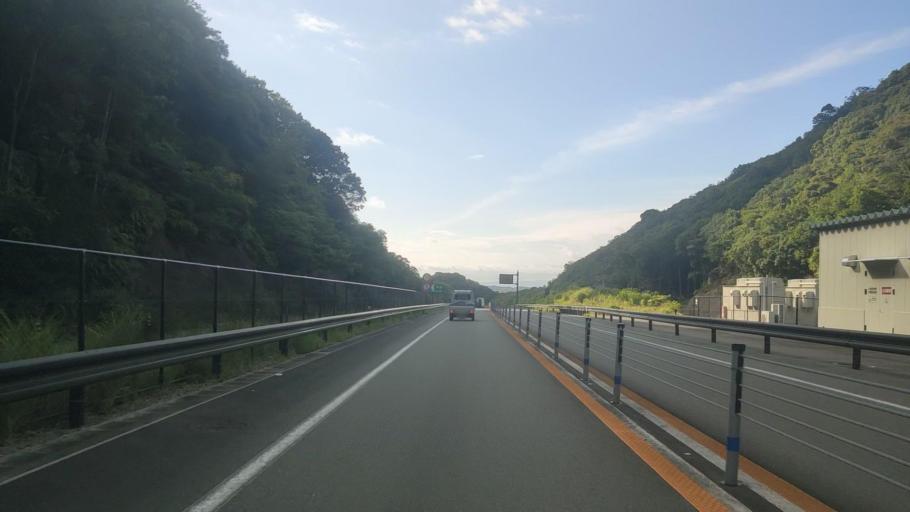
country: JP
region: Wakayama
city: Tanabe
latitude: 33.6329
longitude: 135.4126
